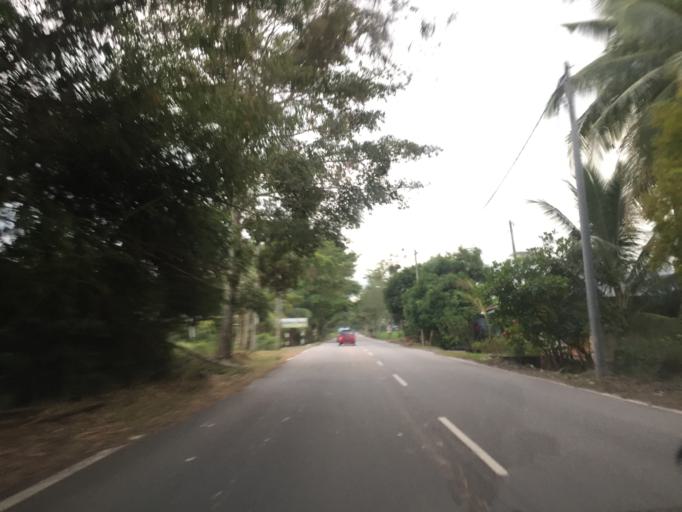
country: MY
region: Penang
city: Tasek Glugor
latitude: 5.5472
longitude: 100.5059
